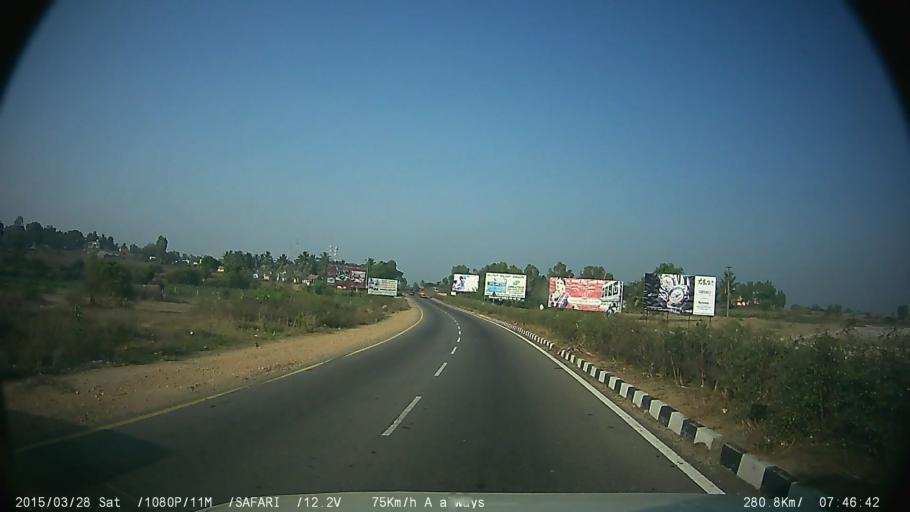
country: IN
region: Karnataka
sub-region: Mandya
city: Pandavapura
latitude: 12.4904
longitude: 76.7839
